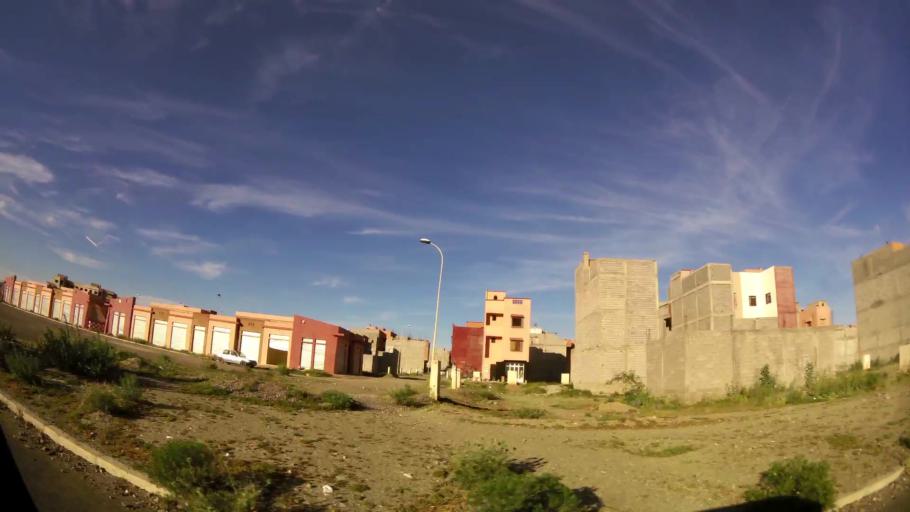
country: MA
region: Marrakech-Tensift-Al Haouz
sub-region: Marrakech
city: Marrakesh
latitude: 31.7618
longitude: -8.1042
